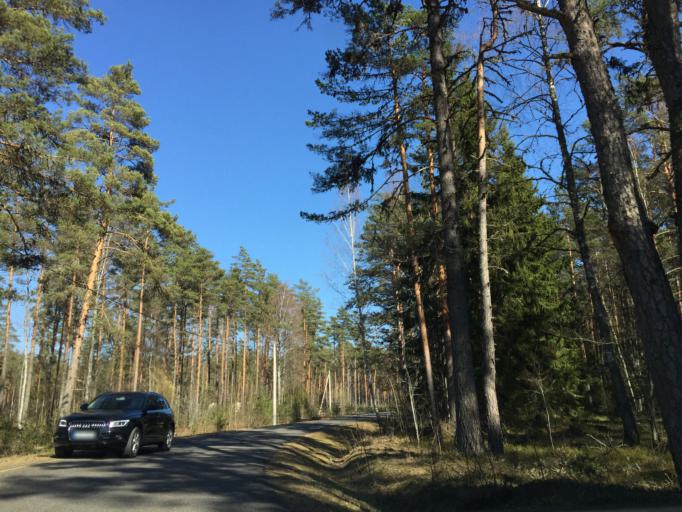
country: EE
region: Jogevamaa
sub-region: Mustvee linn
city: Mustvee
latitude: 58.9915
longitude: 27.2357
